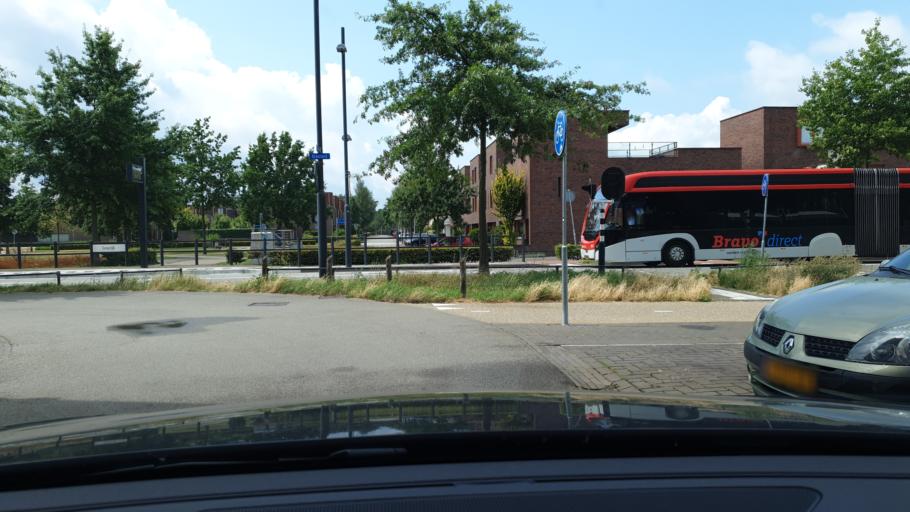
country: NL
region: North Brabant
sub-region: Gemeente Eindhoven
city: Meerhoven
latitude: 51.4398
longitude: 5.4149
